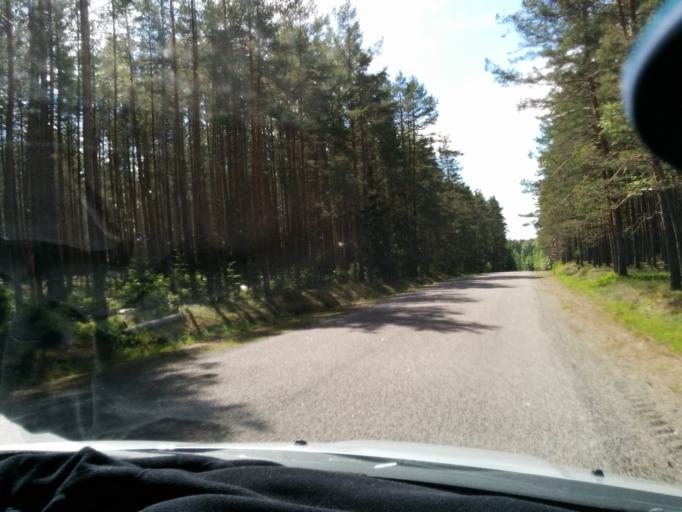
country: EE
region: Harju
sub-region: Loksa linn
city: Loksa
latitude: 59.5266
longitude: 25.9635
